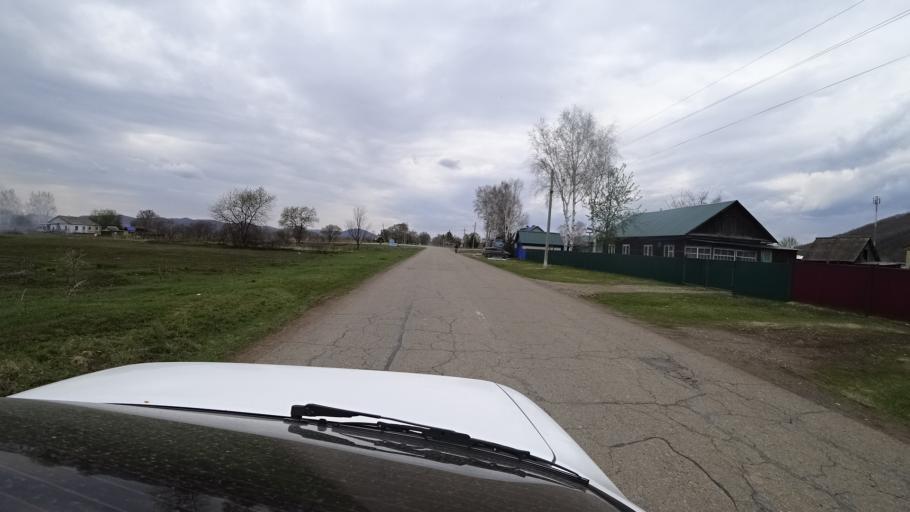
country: RU
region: Primorskiy
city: Novopokrovka
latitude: 45.5772
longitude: 134.3137
